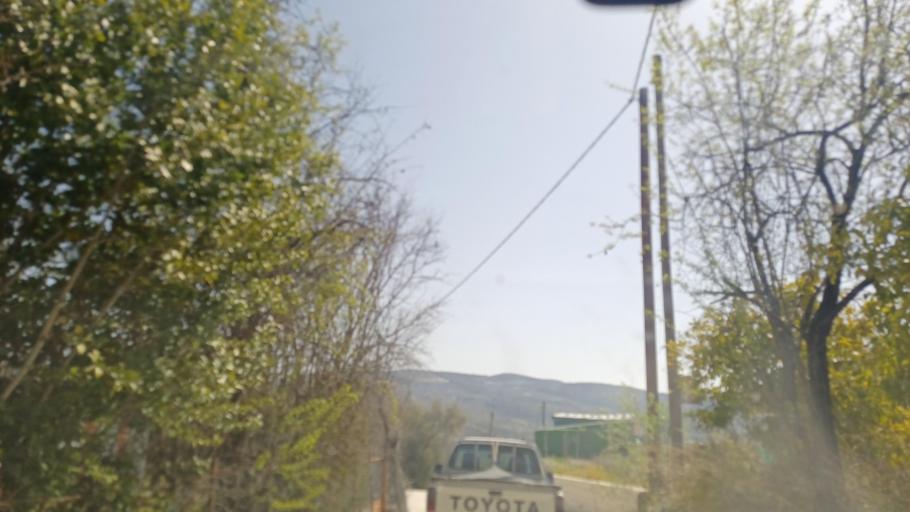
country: CY
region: Limassol
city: Pachna
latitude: 34.8635
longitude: 32.7182
